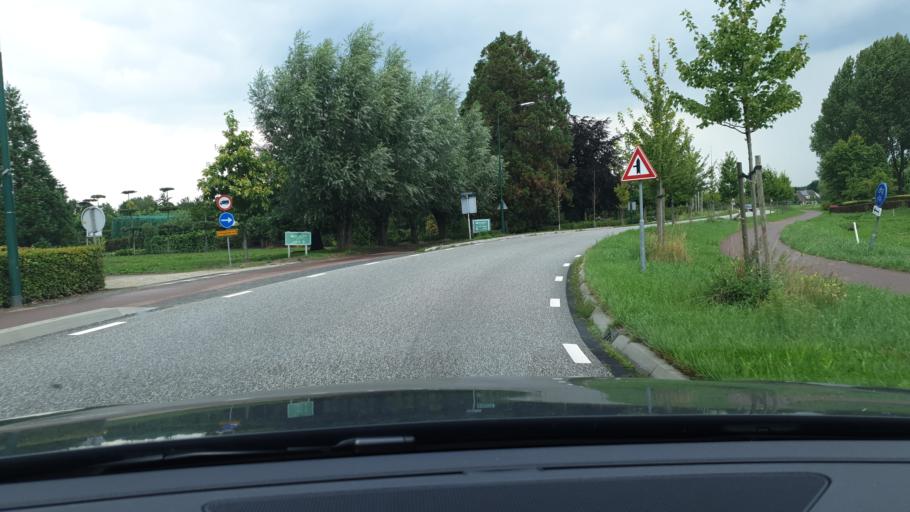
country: NL
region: North Brabant
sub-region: Gemeente Best
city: Best
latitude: 51.5443
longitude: 5.4172
